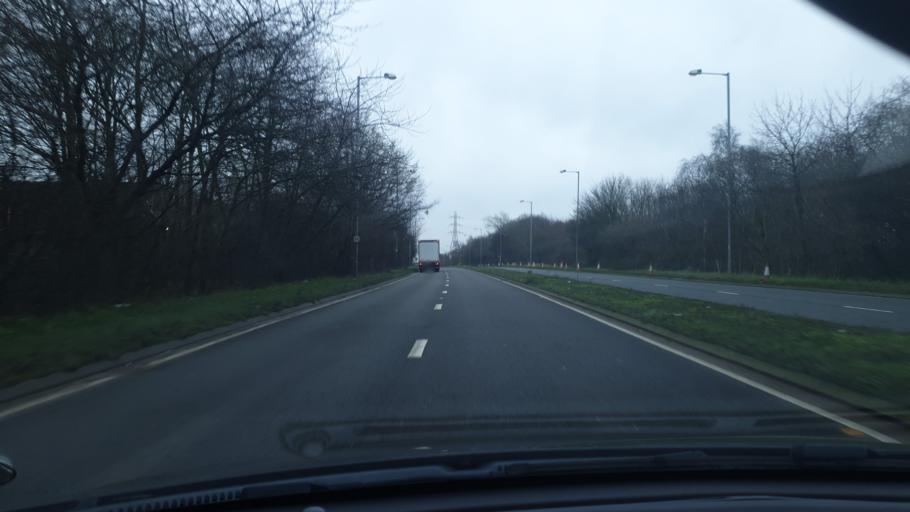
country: GB
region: England
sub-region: Walsall
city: Willenhall
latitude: 52.5807
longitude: -2.0636
